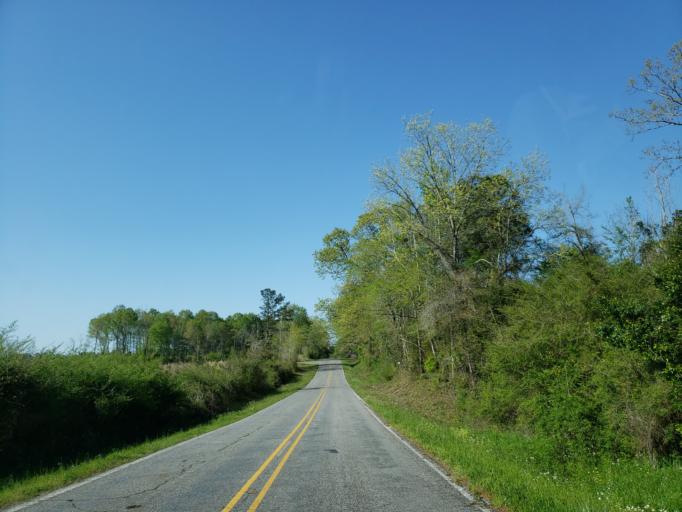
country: US
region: Mississippi
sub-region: Forrest County
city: Rawls Springs
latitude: 31.5180
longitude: -89.3592
